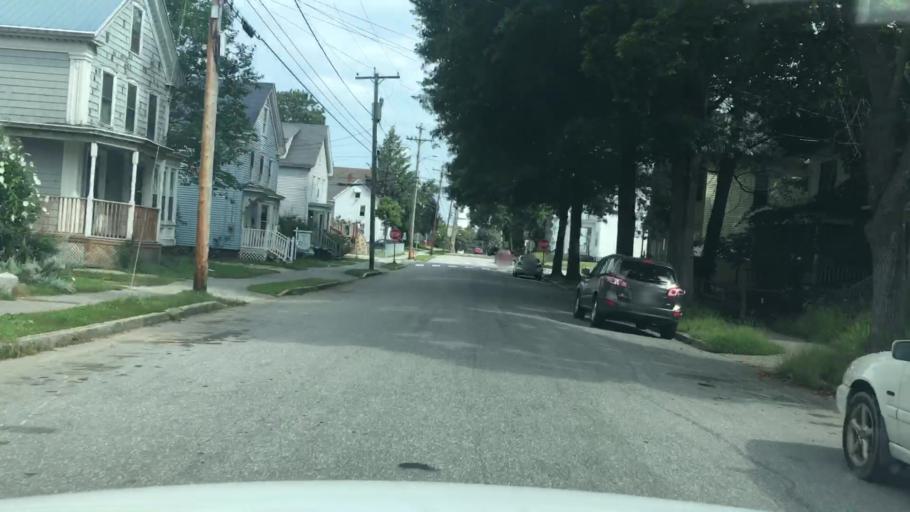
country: US
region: Maine
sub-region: Androscoggin County
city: Auburn
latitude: 44.0947
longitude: -70.2277
